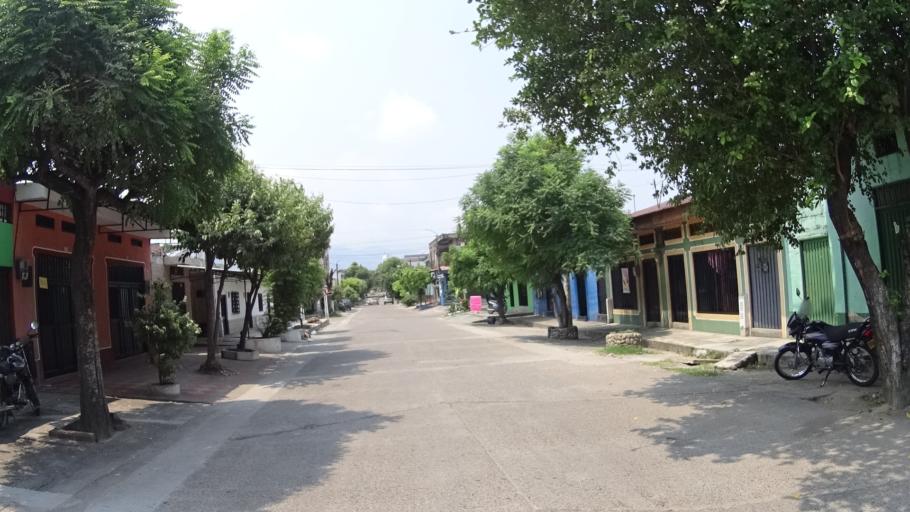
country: CO
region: Caldas
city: La Dorada
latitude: 5.4584
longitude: -74.6652
